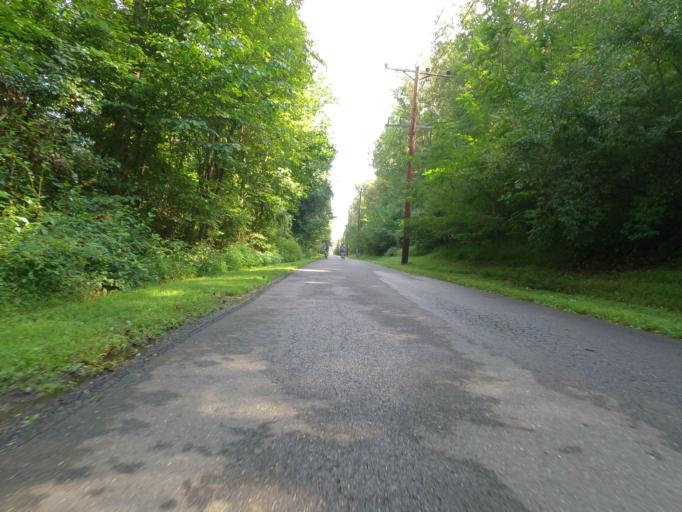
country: US
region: Maryland
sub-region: Anne Arundel County
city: Crofton
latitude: 39.0338
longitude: -76.7233
